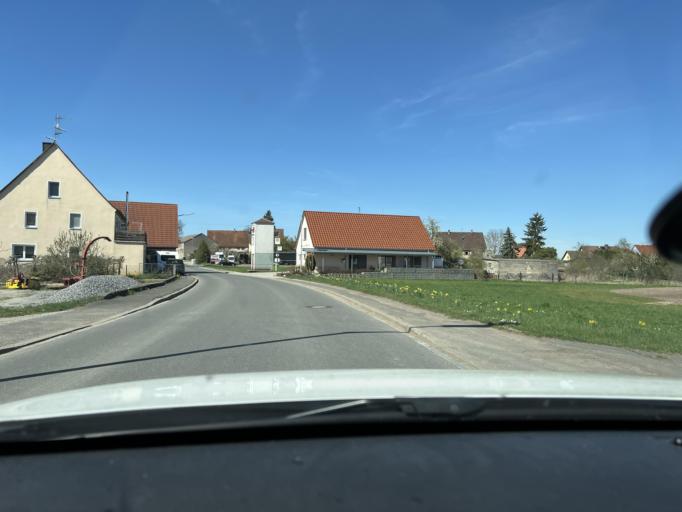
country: DE
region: Bavaria
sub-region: Regierungsbezirk Mittelfranken
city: Wilhermsdorf
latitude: 49.4598
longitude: 10.7370
